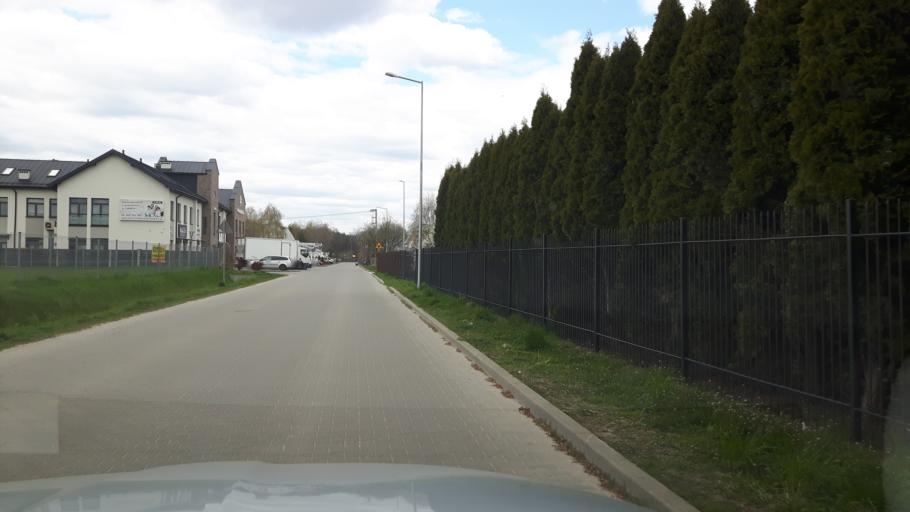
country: PL
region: Masovian Voivodeship
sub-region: Powiat wolominski
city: Kobylka
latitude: 52.3455
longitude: 21.1947
